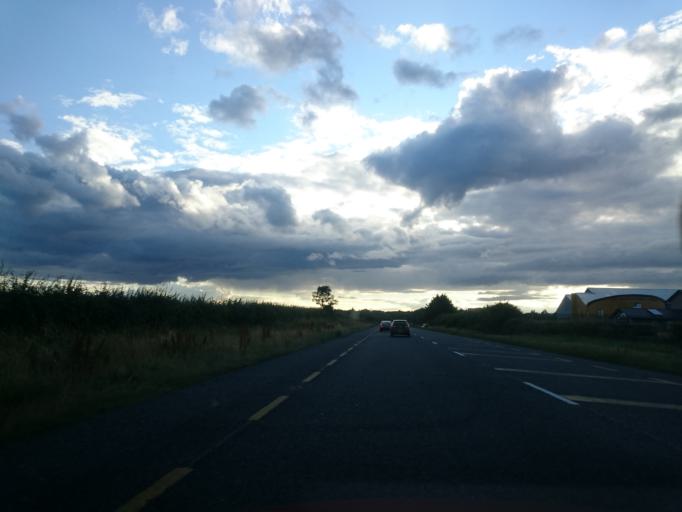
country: IE
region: Leinster
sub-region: Loch Garman
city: Loch Garman
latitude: 52.3031
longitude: -6.4605
